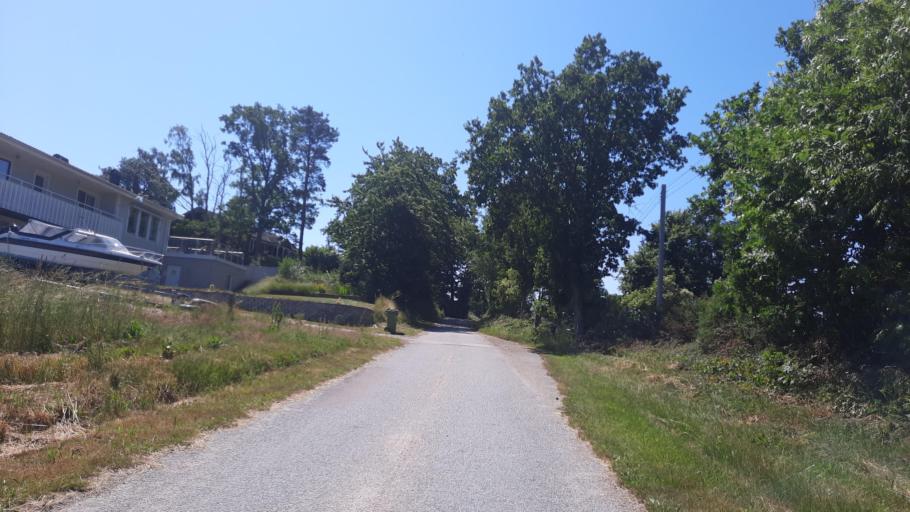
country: SE
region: Blekinge
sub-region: Karlskrona Kommun
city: Jaemjoe
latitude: 56.1545
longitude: 15.7586
